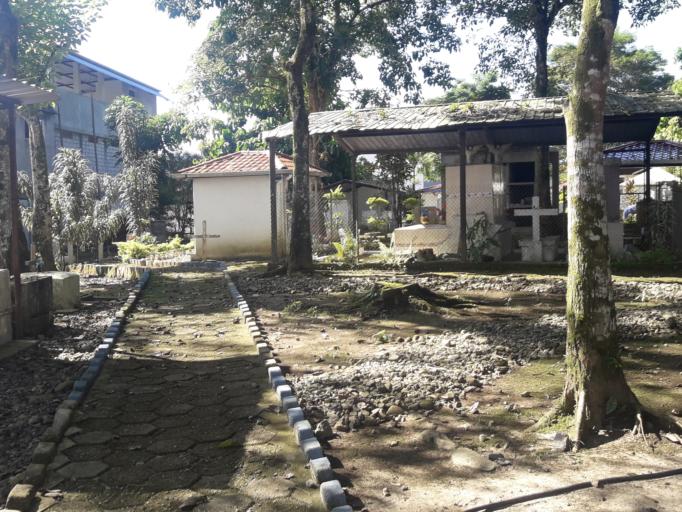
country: EC
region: Napo
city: Tena
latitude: -0.9894
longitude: -77.8184
